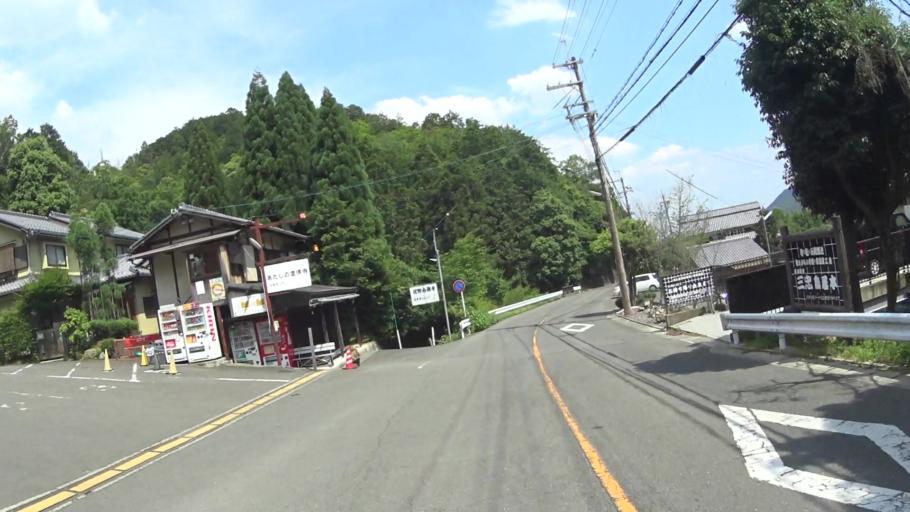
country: JP
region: Kyoto
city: Muko
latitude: 35.0280
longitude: 135.6653
